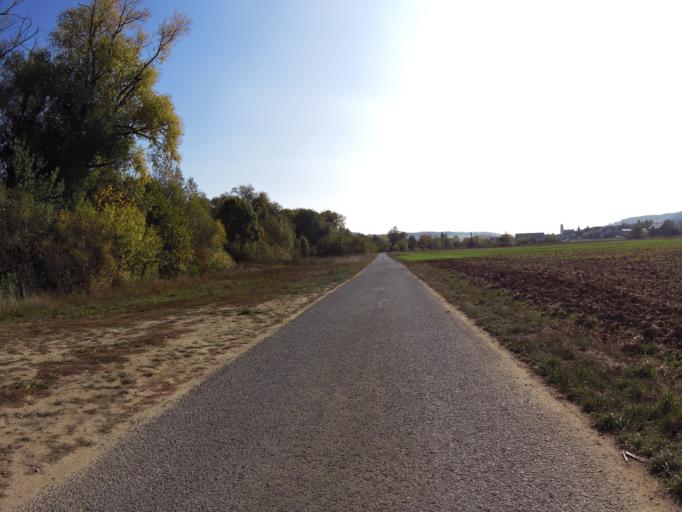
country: DE
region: Bavaria
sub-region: Regierungsbezirk Unterfranken
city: Winterhausen
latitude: 49.7156
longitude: 10.0098
